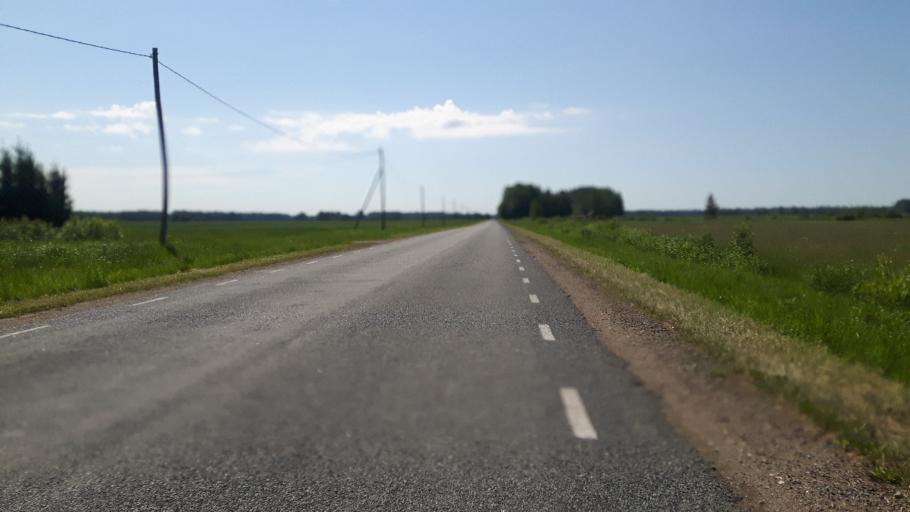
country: EE
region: Paernumaa
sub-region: Vaendra vald (alev)
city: Vandra
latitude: 58.6245
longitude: 25.0210
